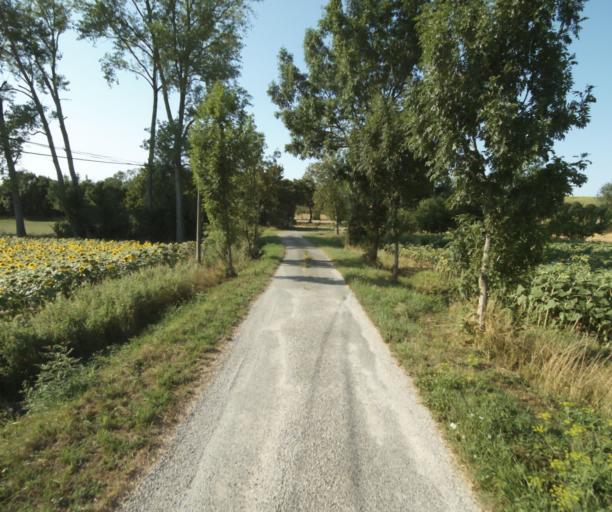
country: FR
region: Midi-Pyrenees
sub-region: Departement de la Haute-Garonne
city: Saint-Felix-Lauragais
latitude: 43.4437
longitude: 1.8122
